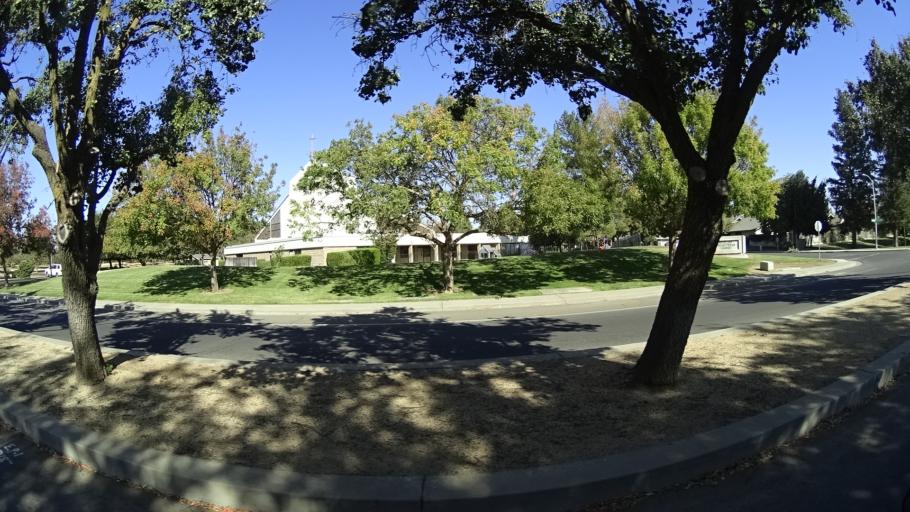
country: US
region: California
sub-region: Yolo County
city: Woodland
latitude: 38.6631
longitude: -121.8018
